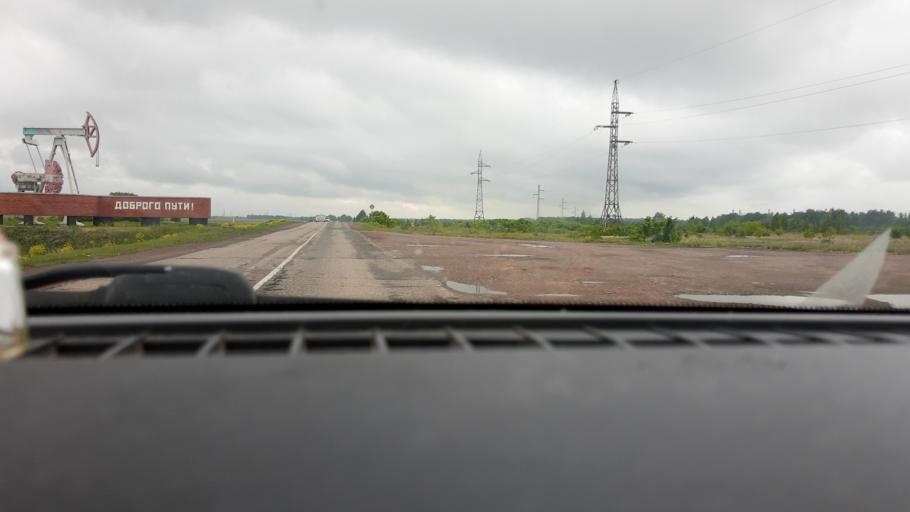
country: RU
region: Bashkortostan
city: Priyutovo
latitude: 53.9205
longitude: 53.9582
